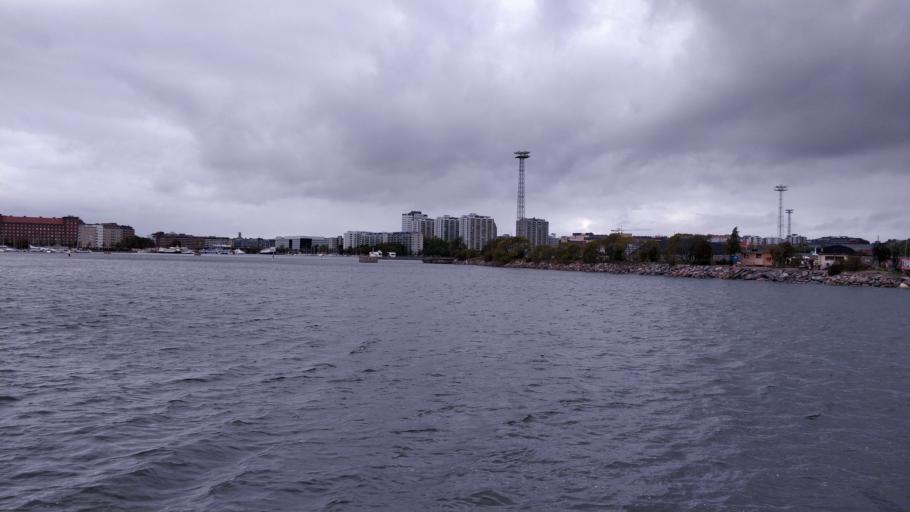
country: FI
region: Uusimaa
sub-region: Helsinki
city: Helsinki
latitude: 60.1749
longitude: 24.9768
